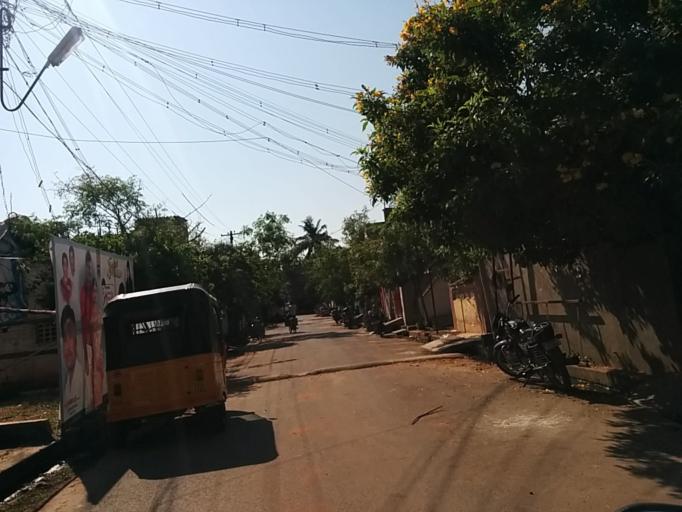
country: IN
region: Pondicherry
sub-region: Puducherry
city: Puducherry
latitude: 11.9620
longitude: 79.8279
